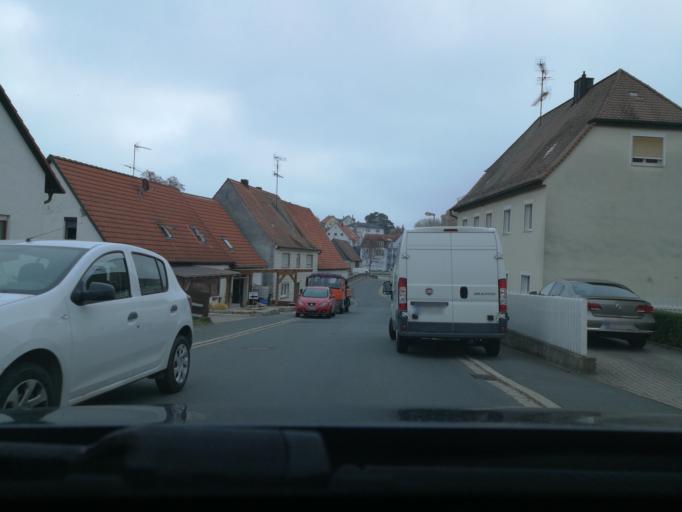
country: DE
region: Bavaria
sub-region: Regierungsbezirk Mittelfranken
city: Weisendorf
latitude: 49.5747
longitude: 10.8232
